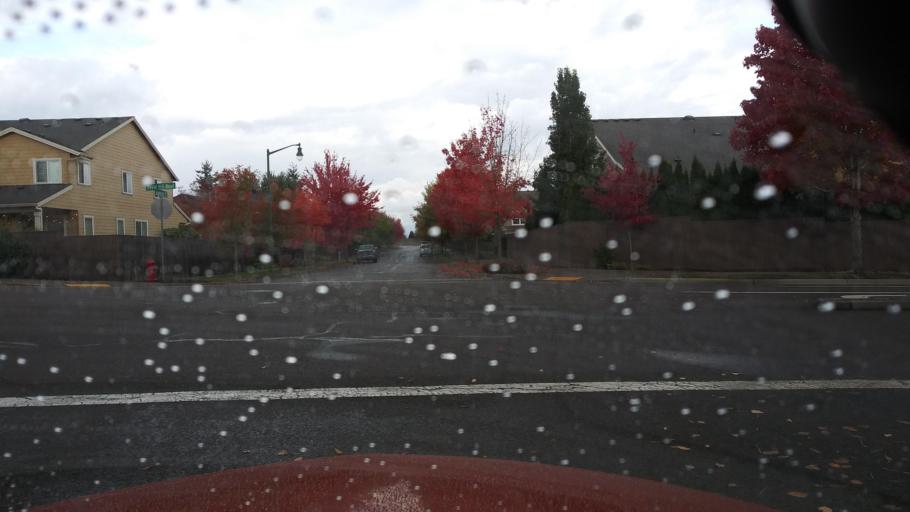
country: US
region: Oregon
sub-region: Washington County
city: Forest Grove
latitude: 45.5391
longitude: -123.1286
